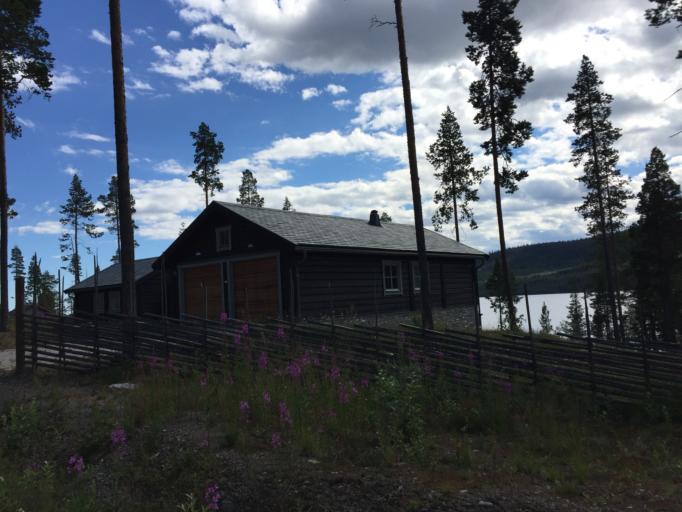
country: SE
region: Jaemtland
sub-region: Harjedalens Kommun
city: Sveg
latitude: 62.1102
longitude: 13.2938
